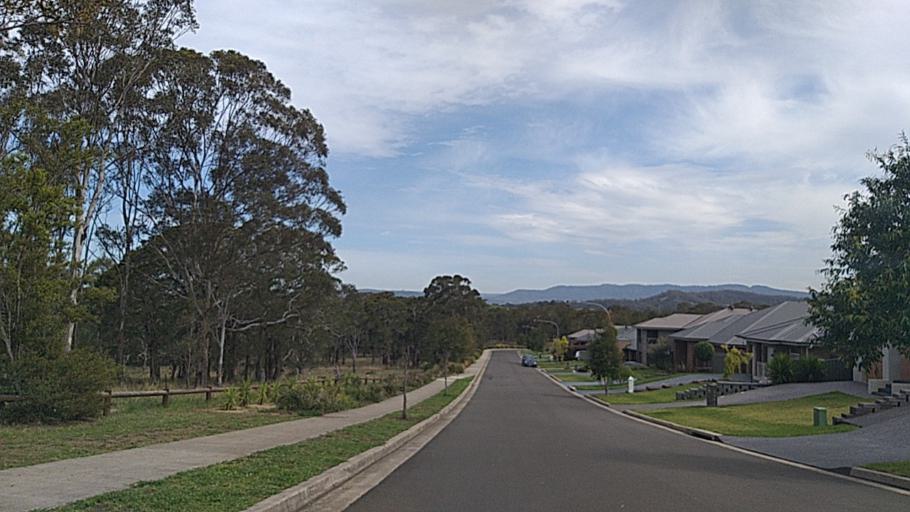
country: AU
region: New South Wales
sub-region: Wollongong
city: Dapto
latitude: -34.4943
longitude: 150.7632
